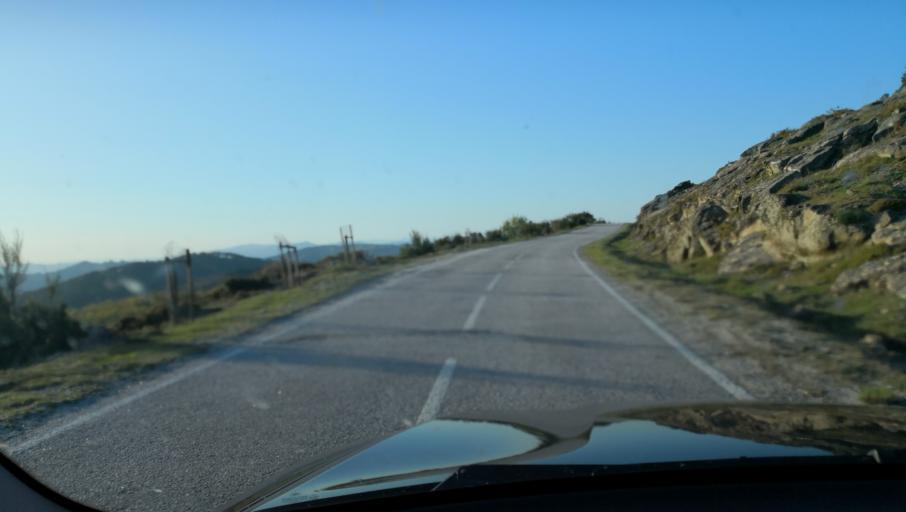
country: PT
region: Vila Real
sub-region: Vila Real
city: Vila Real
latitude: 41.3890
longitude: -7.8271
